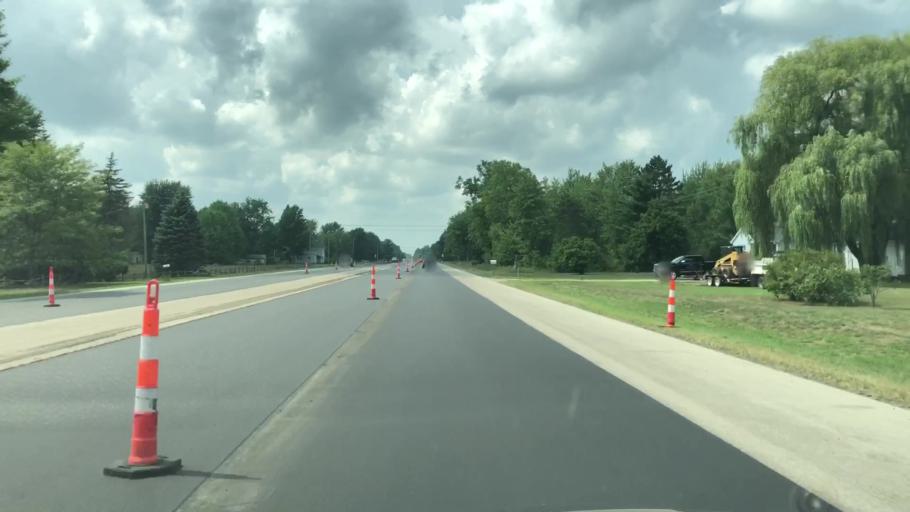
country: US
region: Michigan
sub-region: Isabella County
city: Shepherd
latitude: 43.6120
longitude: -84.6732
